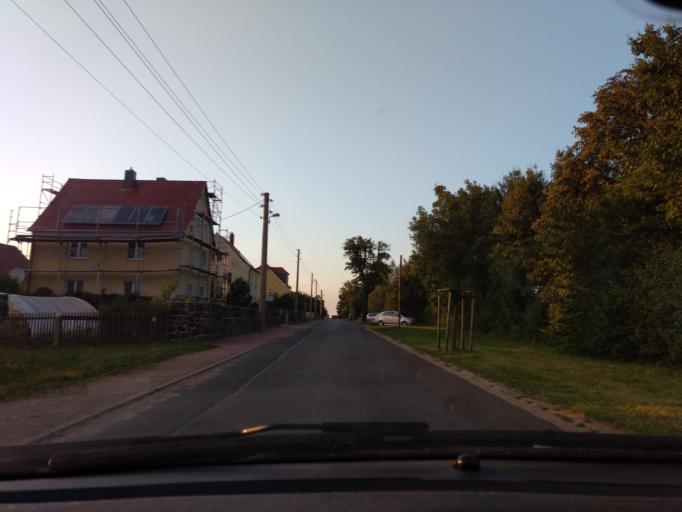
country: DE
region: Saxony
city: Radebeul
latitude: 51.1168
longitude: 13.6690
